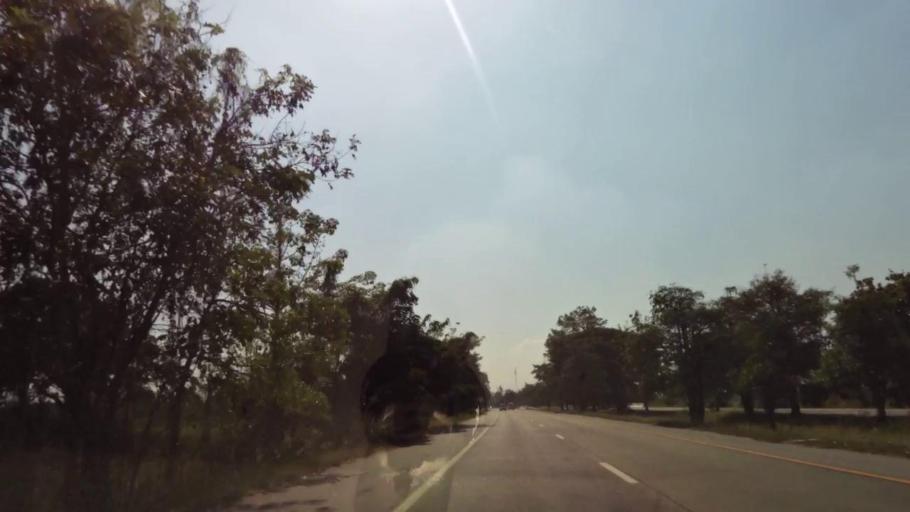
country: TH
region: Phitsanulok
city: Bang Rakam
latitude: 16.6437
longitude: 100.1499
